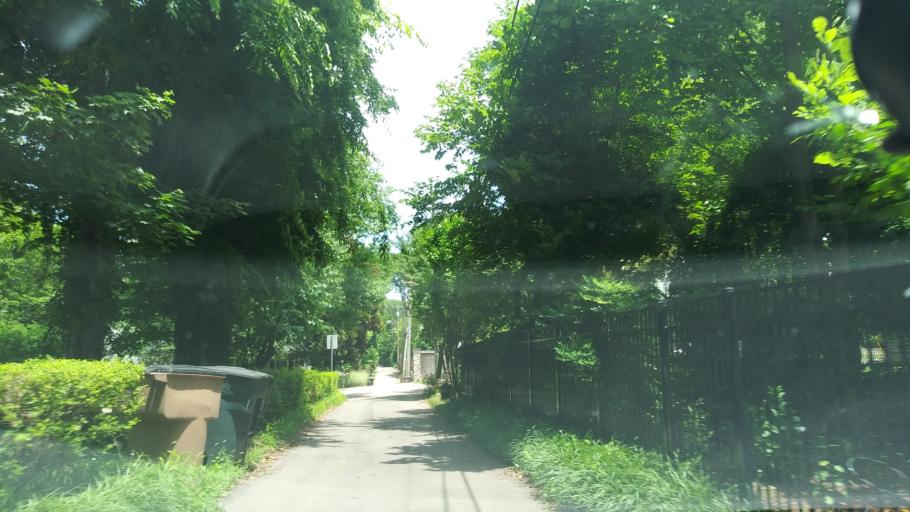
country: US
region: Tennessee
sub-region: Davidson County
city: Belle Meade
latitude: 36.1365
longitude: -86.8297
